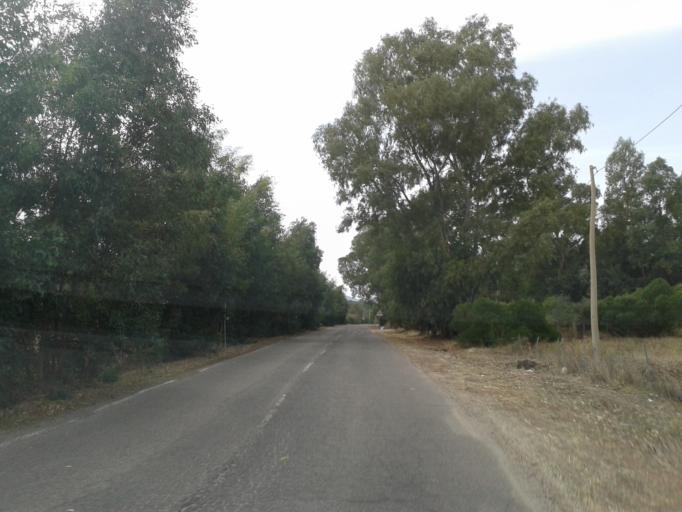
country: IT
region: Sardinia
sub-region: Provincia di Cagliari
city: Olia Speciosa
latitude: 39.2855
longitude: 9.5759
